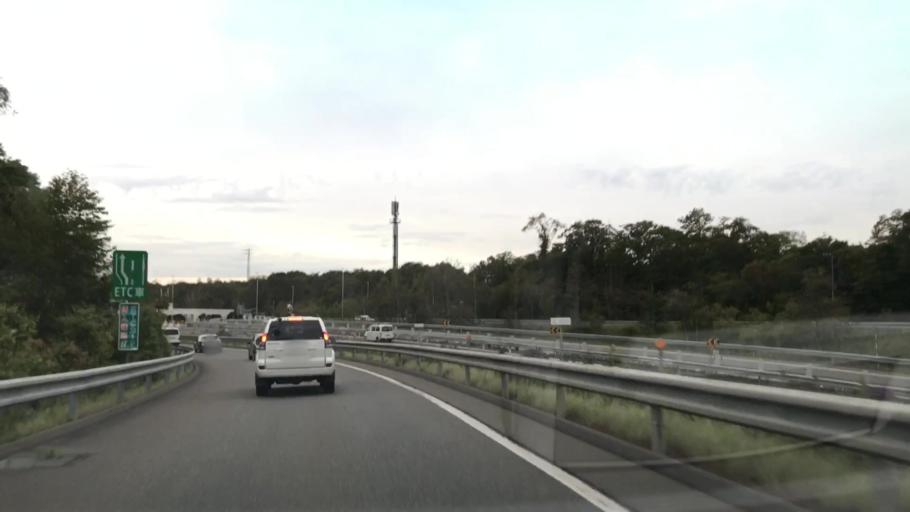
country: JP
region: Hokkaido
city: Tomakomai
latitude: 42.7086
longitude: 141.6581
